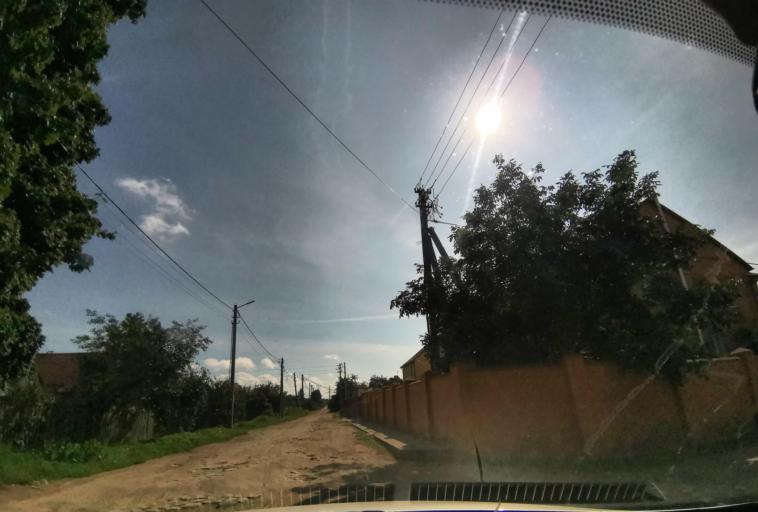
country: RU
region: Kaliningrad
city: Chernyakhovsk
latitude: 54.6598
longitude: 21.8392
